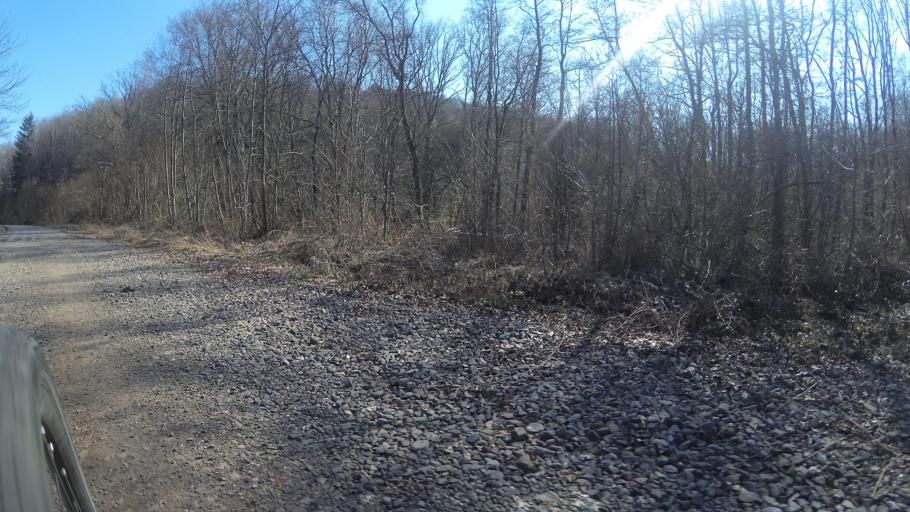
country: DE
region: Rheinland-Pfalz
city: Achtelsbach
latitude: 49.5834
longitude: 7.0759
